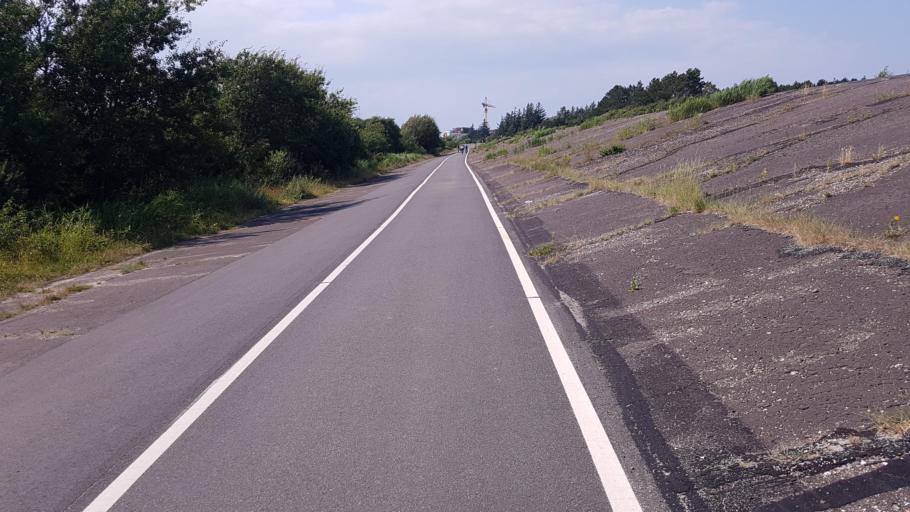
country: DE
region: Schleswig-Holstein
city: Sankt Peter-Ording
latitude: 54.3039
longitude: 8.6252
